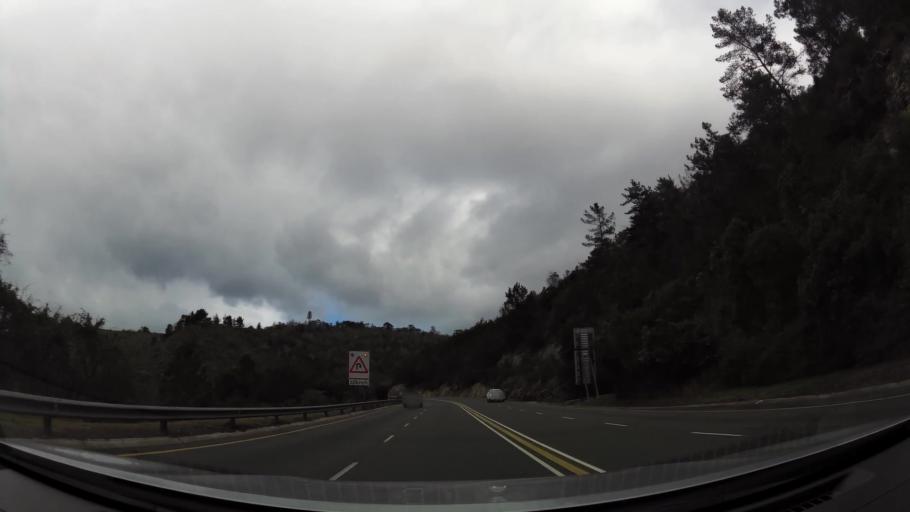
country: ZA
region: Western Cape
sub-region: Eden District Municipality
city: George
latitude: -33.9884
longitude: 22.5498
